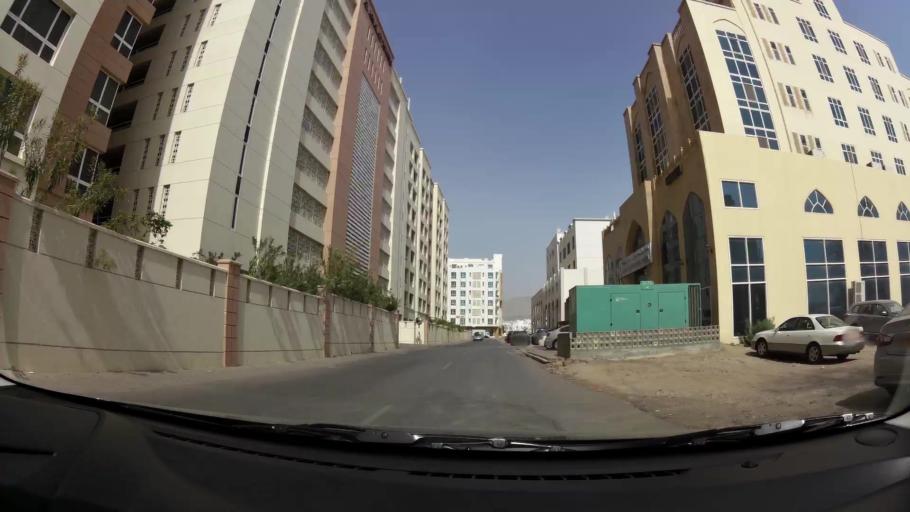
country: OM
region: Muhafazat Masqat
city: Bawshar
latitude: 23.5809
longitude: 58.3976
